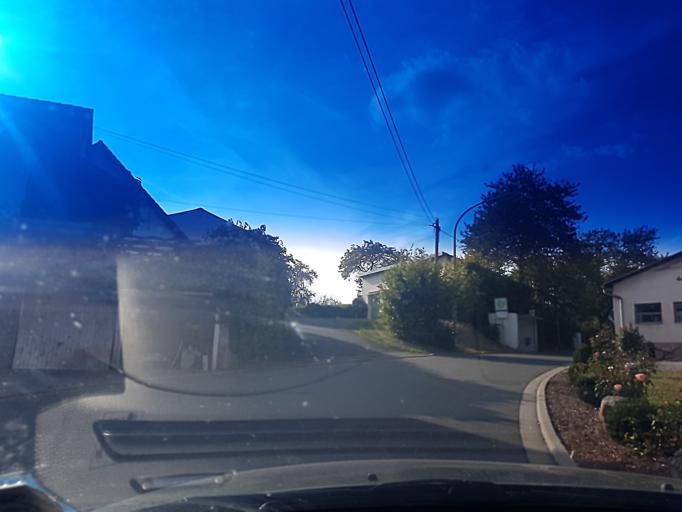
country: DE
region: Bavaria
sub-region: Upper Franconia
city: Schlusselfeld
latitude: 49.7750
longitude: 10.5799
